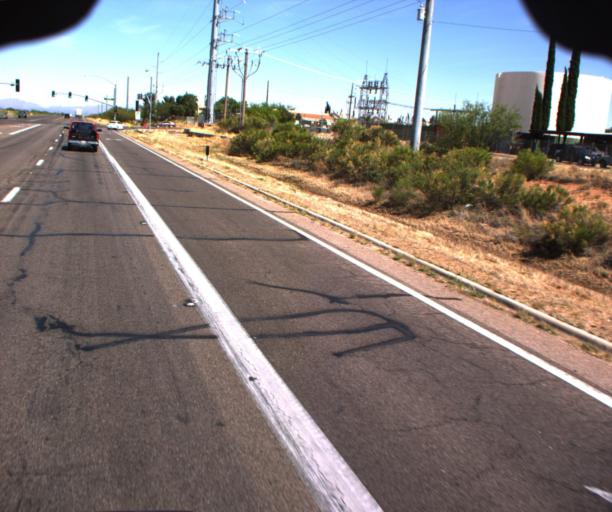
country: US
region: Arizona
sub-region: Cochise County
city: Sierra Vista
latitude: 31.5694
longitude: -110.2927
